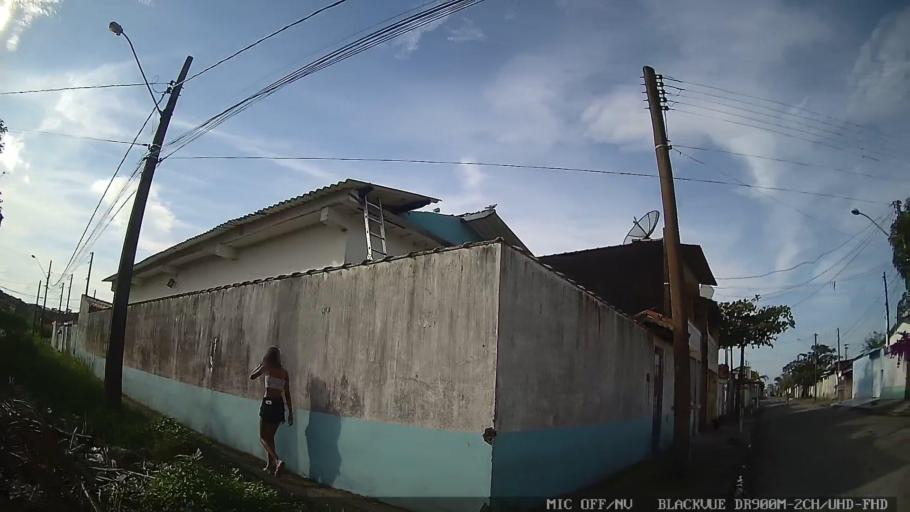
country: BR
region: Sao Paulo
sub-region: Itanhaem
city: Itanhaem
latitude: -24.1620
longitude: -46.7600
